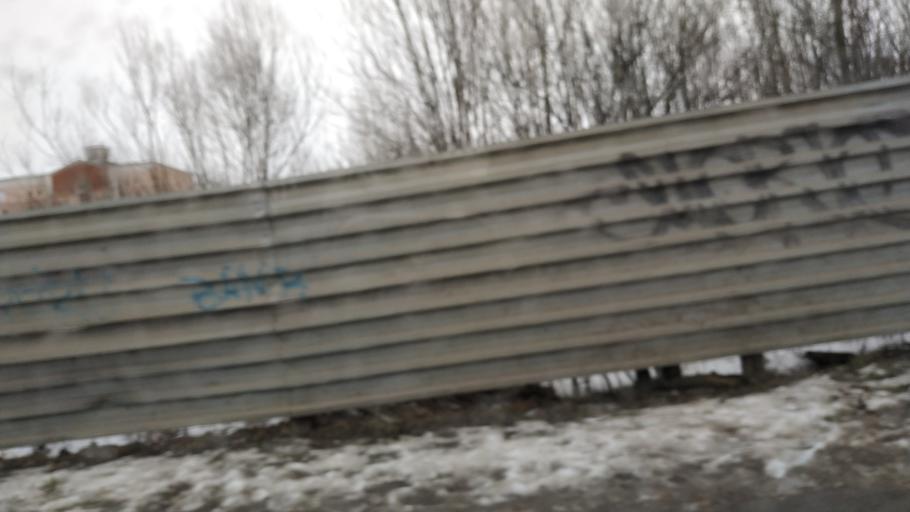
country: RU
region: Tverskaya
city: Tver
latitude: 56.8813
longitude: 35.9001
